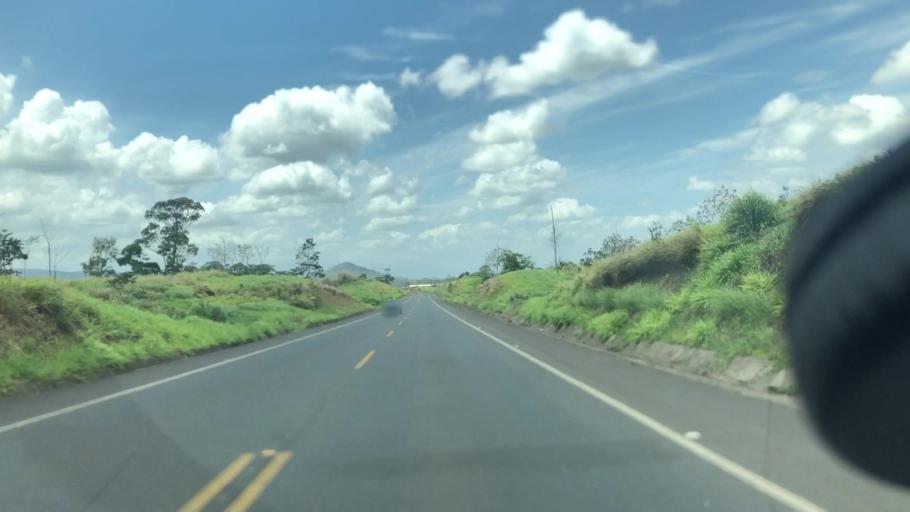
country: CR
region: Alajuela
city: Pital
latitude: 10.4345
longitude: -84.2841
